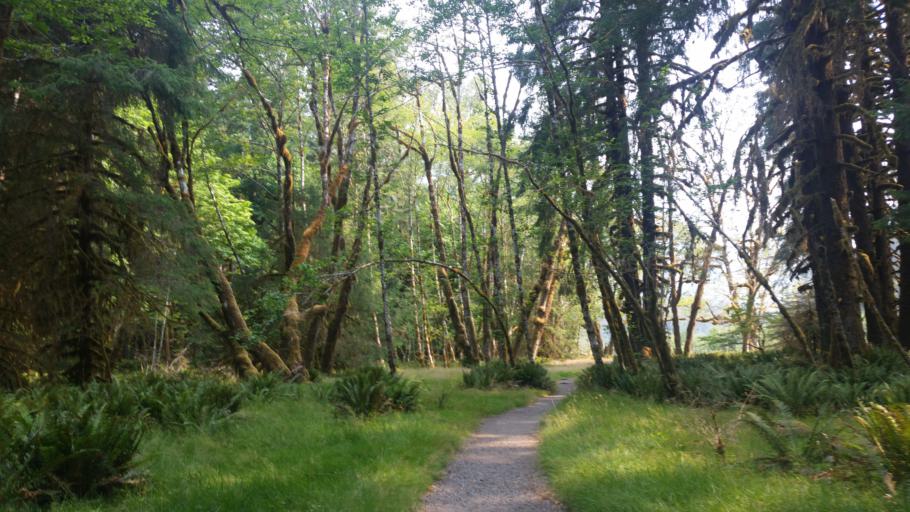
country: US
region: Washington
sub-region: Clallam County
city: Forks
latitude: 47.8603
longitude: -123.9254
